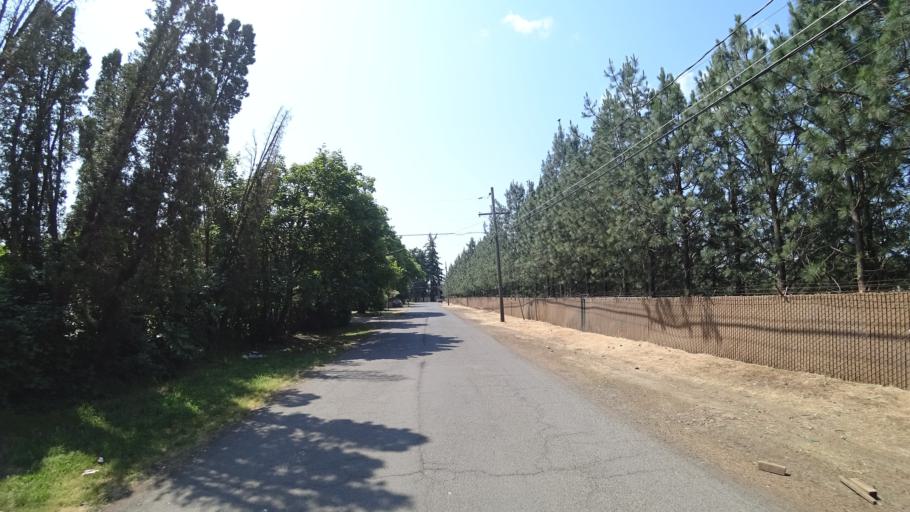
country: US
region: Oregon
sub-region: Multnomah County
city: Lents
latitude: 45.4508
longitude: -122.5827
